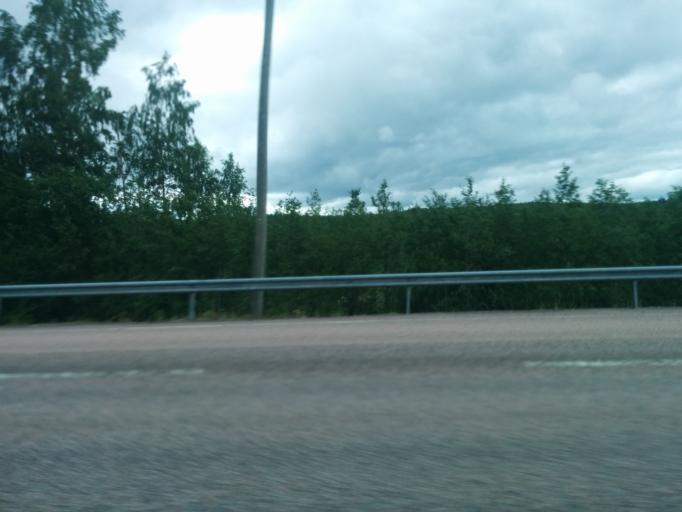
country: FI
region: Pirkanmaa
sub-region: Tampere
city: Orivesi
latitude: 61.7106
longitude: 24.5095
